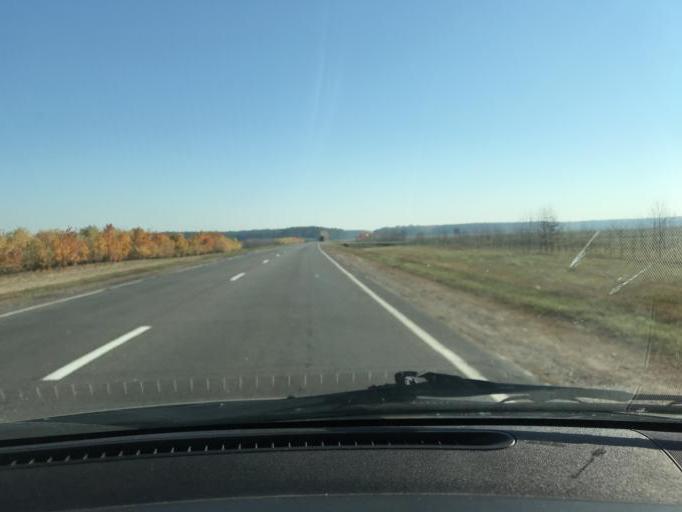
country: BY
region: Brest
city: Luninyets
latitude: 52.2756
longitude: 26.9710
